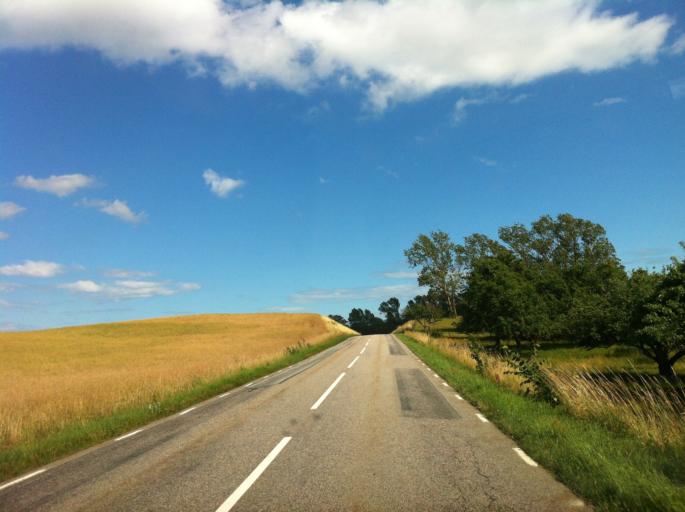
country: SE
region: Skane
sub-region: Ystads Kommun
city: Kopingebro
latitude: 55.4181
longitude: 13.9970
